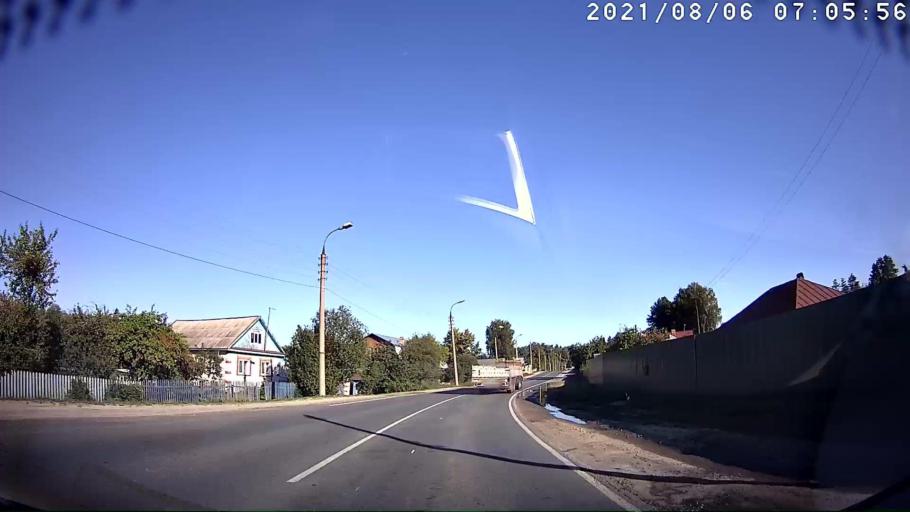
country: RU
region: Mariy-El
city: Yoshkar-Ola
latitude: 56.5560
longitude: 47.9838
